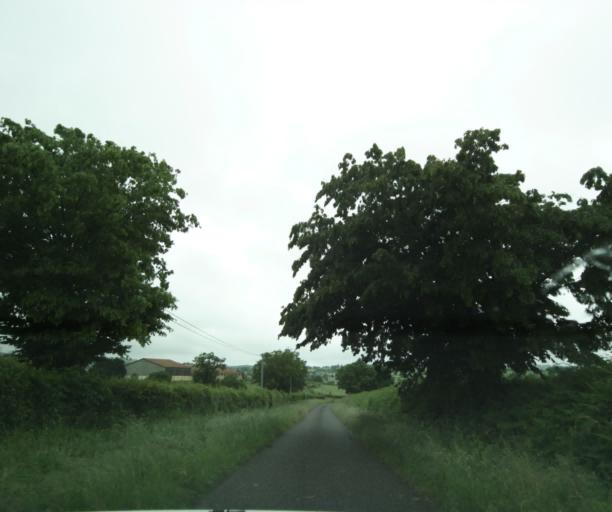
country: FR
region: Bourgogne
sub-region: Departement de Saone-et-Loire
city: La Clayette
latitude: 46.3493
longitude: 4.2309
